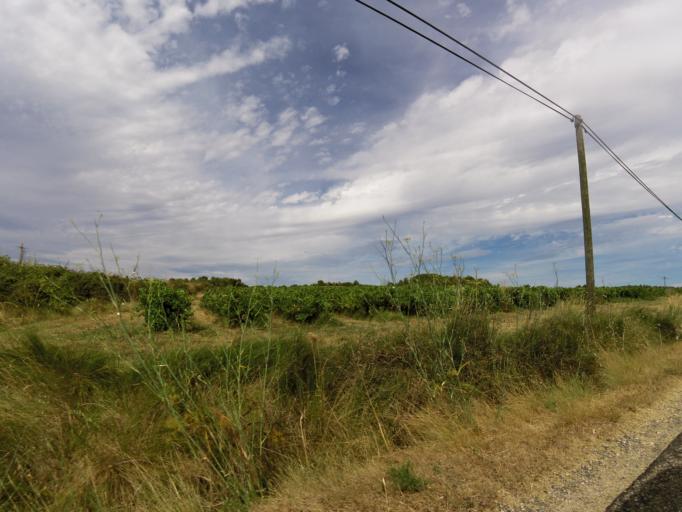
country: FR
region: Languedoc-Roussillon
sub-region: Departement du Gard
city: Villevieille
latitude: 43.8234
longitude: 4.1327
